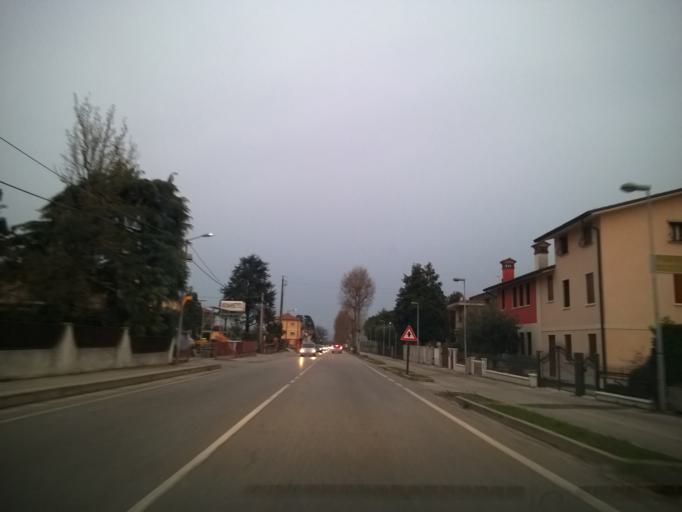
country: IT
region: Veneto
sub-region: Provincia di Vicenza
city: Villaverla
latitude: 45.6729
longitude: 11.4882
